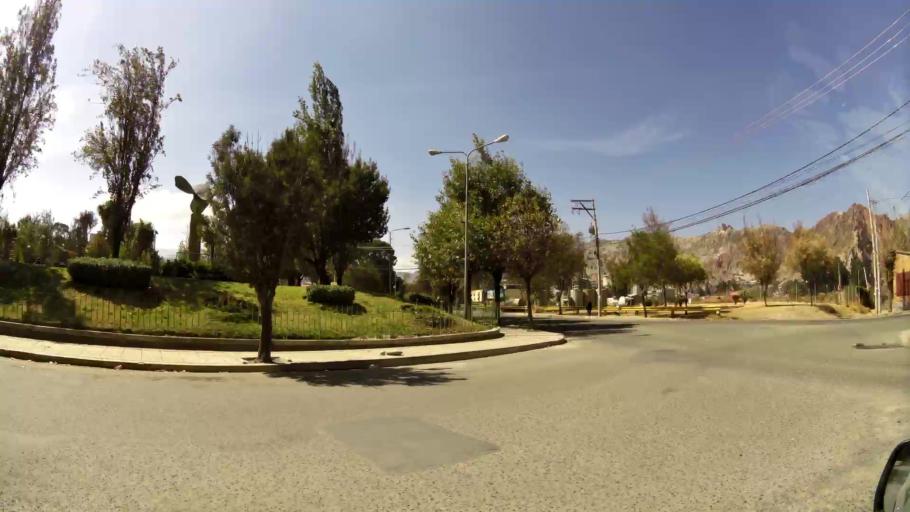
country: BO
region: La Paz
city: La Paz
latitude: -16.5439
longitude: -68.0944
